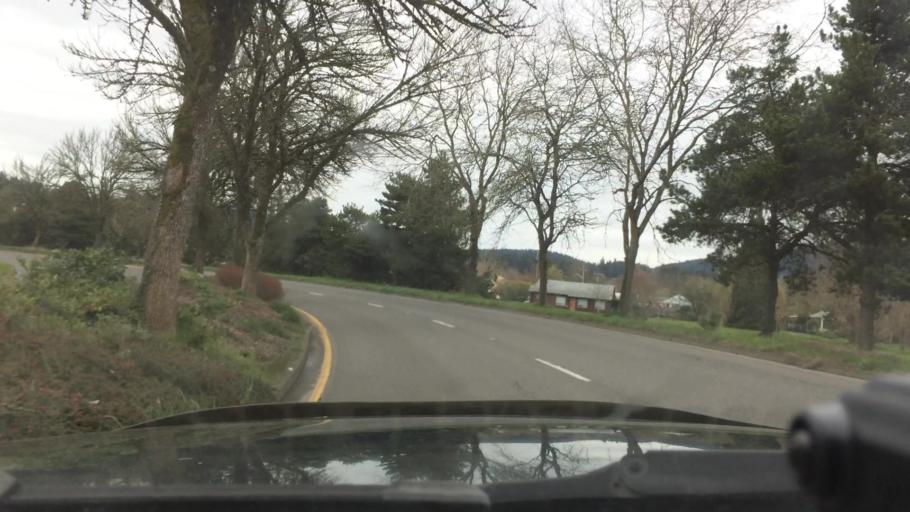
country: US
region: Oregon
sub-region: Lane County
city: Eugene
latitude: 44.0253
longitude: -123.0846
